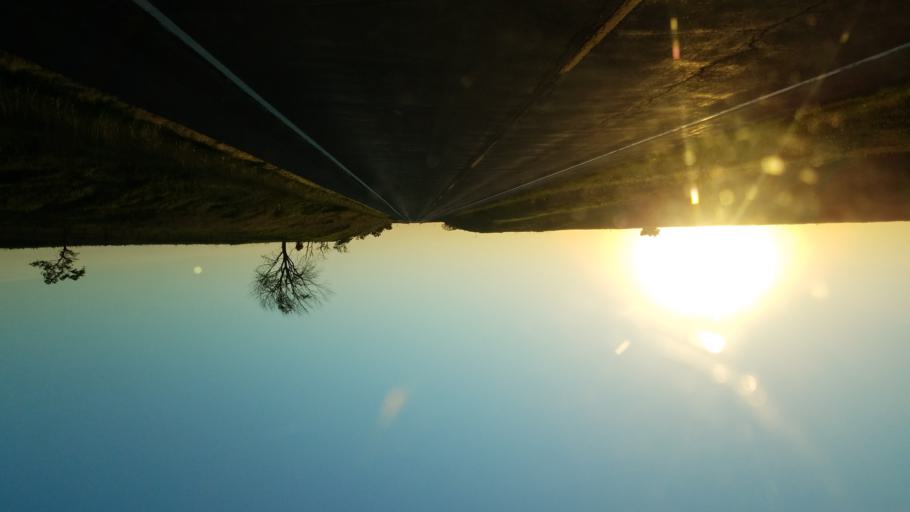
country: US
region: Missouri
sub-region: Schuyler County
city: Lancaster
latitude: 40.4926
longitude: -92.5854
